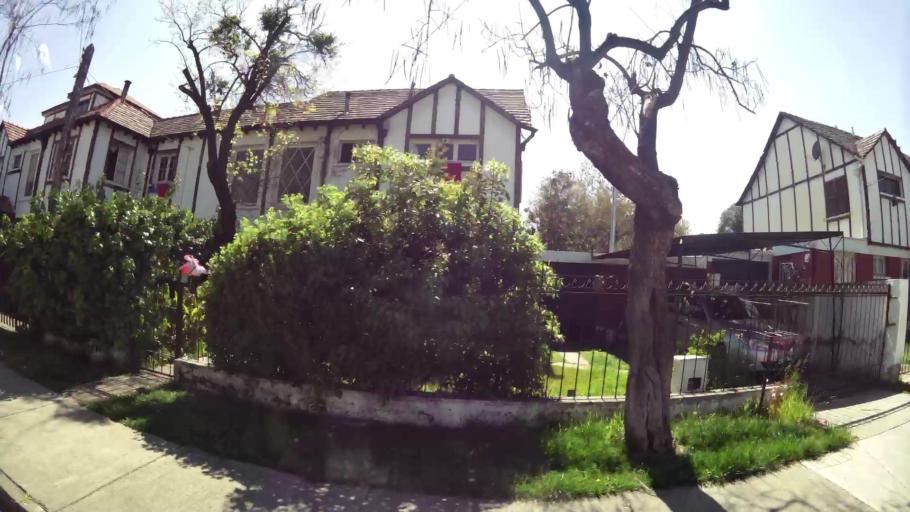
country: CL
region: Santiago Metropolitan
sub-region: Provincia de Santiago
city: Villa Presidente Frei, Nunoa, Santiago, Chile
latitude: -33.4143
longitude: -70.5668
